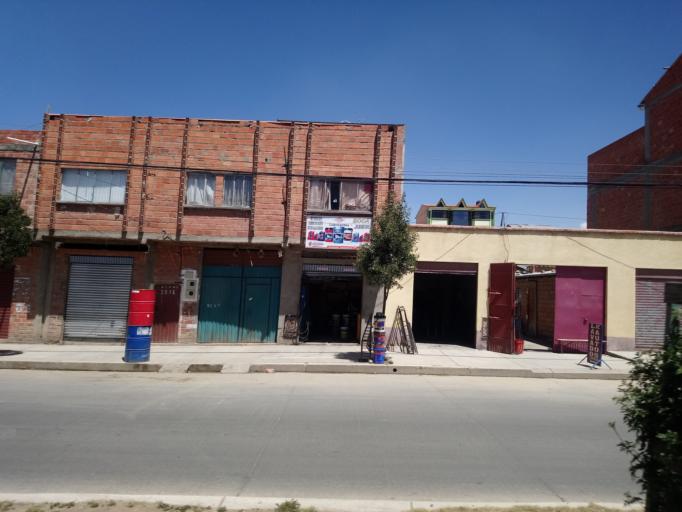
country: BO
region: La Paz
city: La Paz
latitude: -16.5388
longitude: -68.1864
